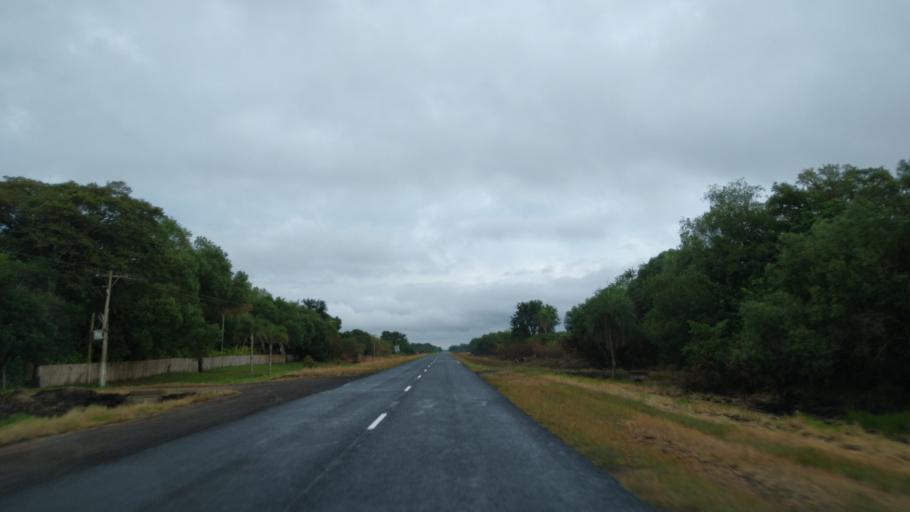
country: AR
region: Corrientes
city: Loreto
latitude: -27.7475
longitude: -57.2535
